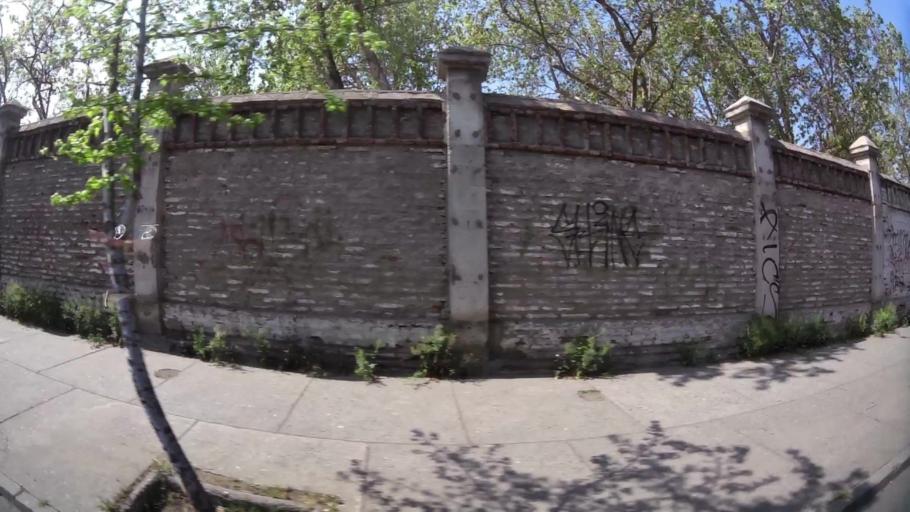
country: CL
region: Santiago Metropolitan
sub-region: Provincia de Santiago
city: Santiago
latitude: -33.4592
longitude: -70.6719
